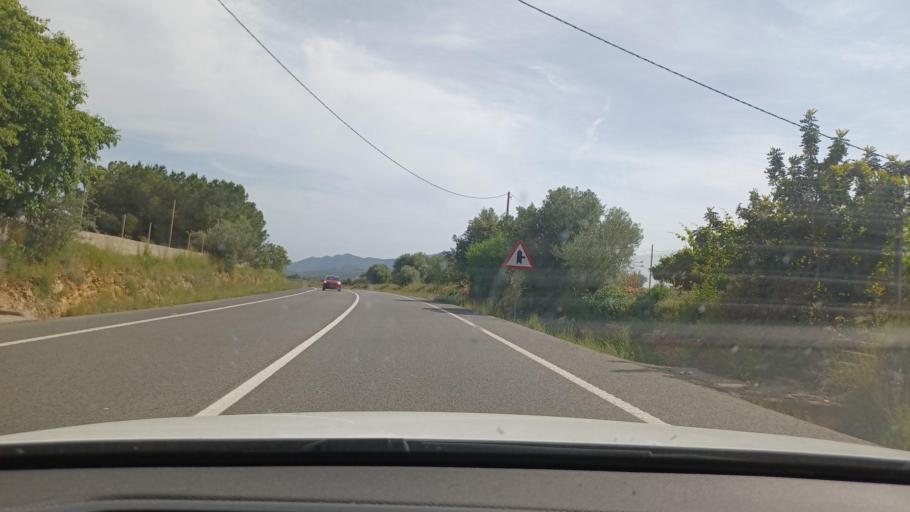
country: ES
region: Catalonia
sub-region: Provincia de Tarragona
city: Amposta
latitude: 40.7182
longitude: 0.5636
